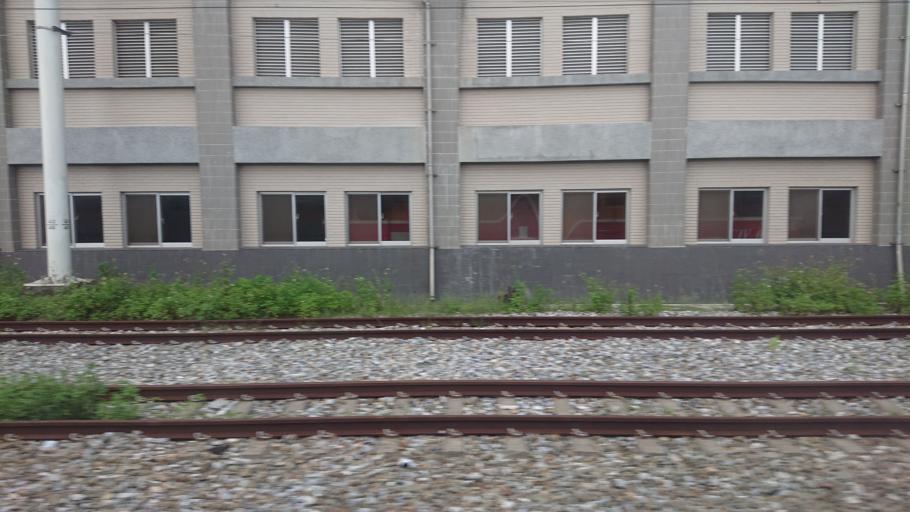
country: TW
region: Taiwan
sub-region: Hualien
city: Hualian
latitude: 23.6653
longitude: 121.4205
